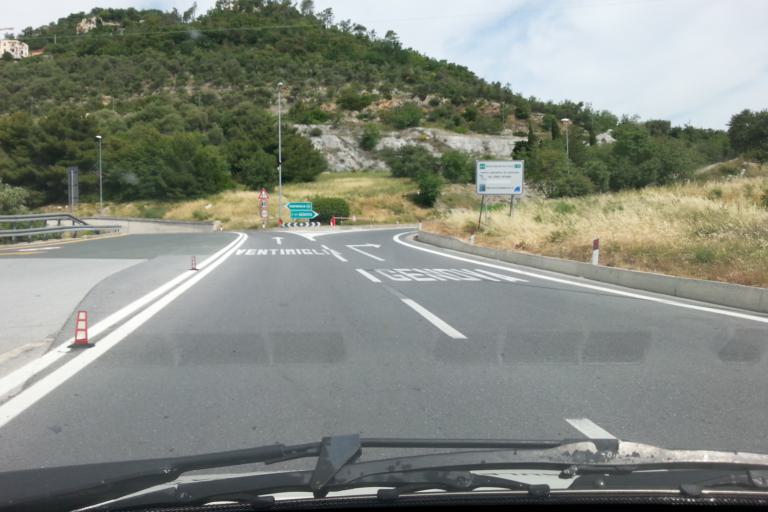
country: IT
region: Liguria
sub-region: Provincia di Savona
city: Pietra Ligure
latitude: 44.1555
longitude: 8.2708
